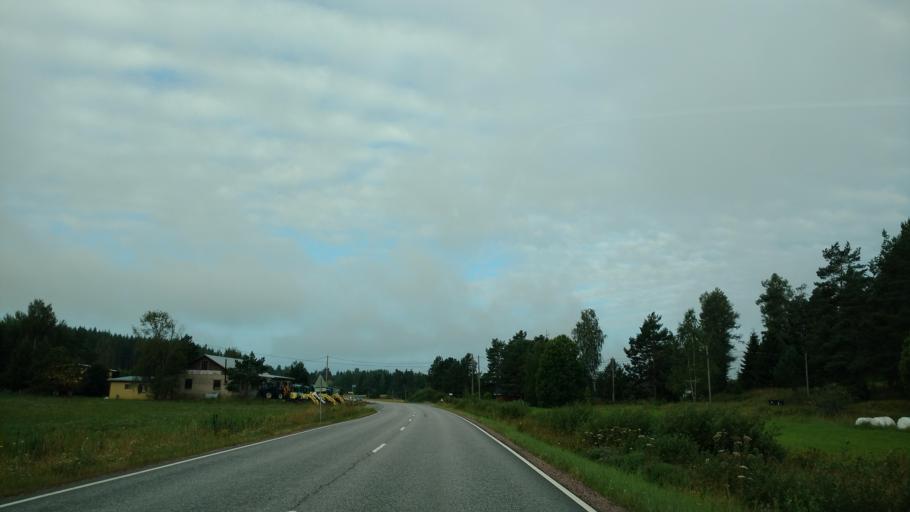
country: FI
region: Varsinais-Suomi
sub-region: Aboland-Turunmaa
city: Kimito
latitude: 60.1451
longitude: 22.6840
